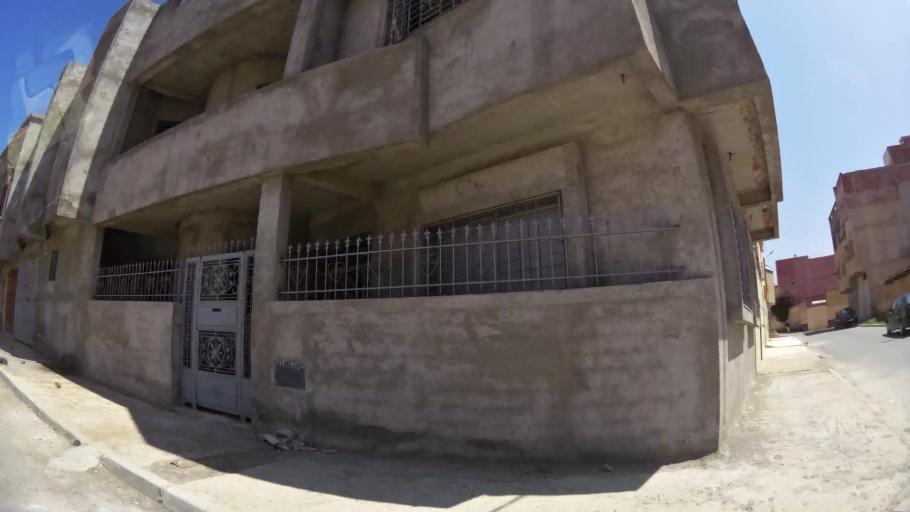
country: MA
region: Oriental
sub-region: Oujda-Angad
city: Oujda
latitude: 34.6924
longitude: -1.8853
